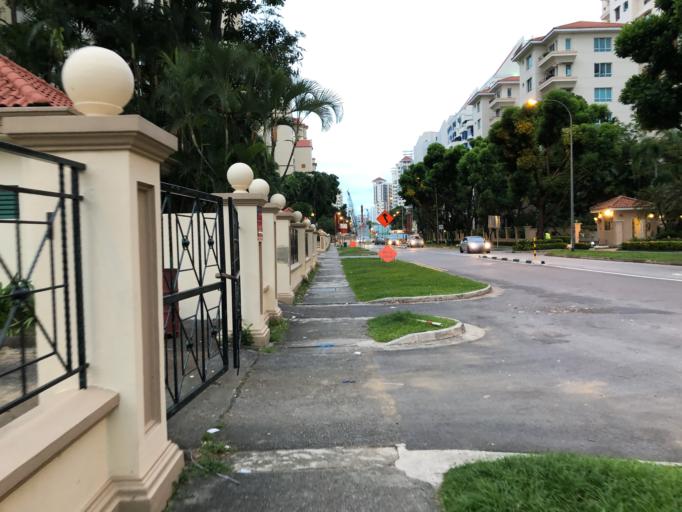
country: SG
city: Singapore
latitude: 1.2972
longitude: 103.8700
